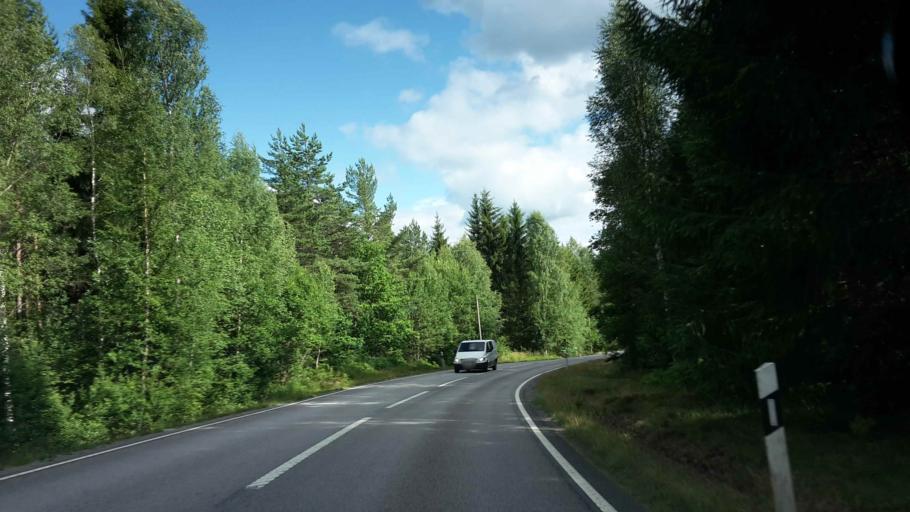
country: SE
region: OErebro
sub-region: Hallsbergs Kommun
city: Palsboda
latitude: 58.8047
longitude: 15.4204
